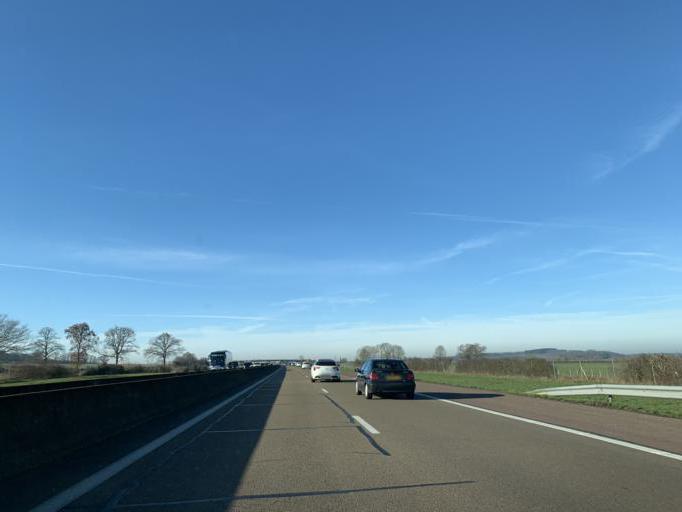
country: FR
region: Bourgogne
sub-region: Departement de l'Yonne
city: Avallon
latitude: 47.5050
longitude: 4.0521
